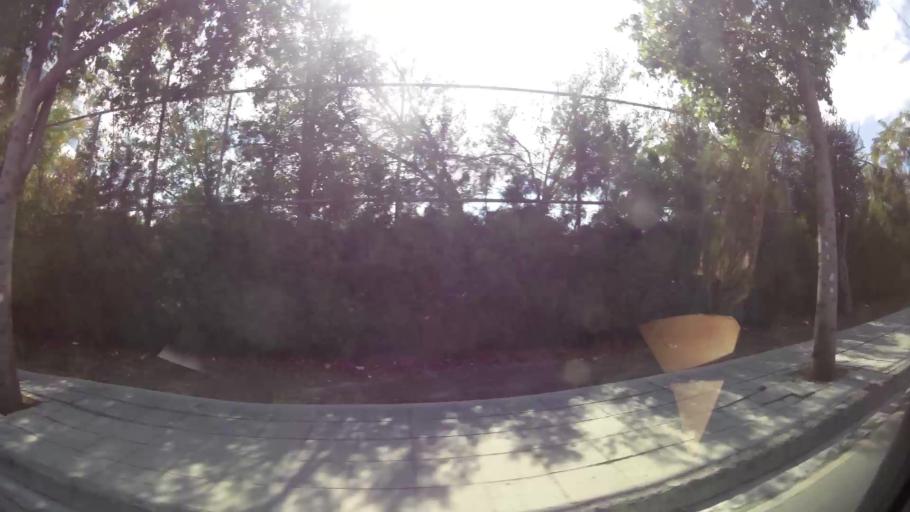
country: CY
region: Lefkosia
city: Nicosia
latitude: 35.1864
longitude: 33.3878
